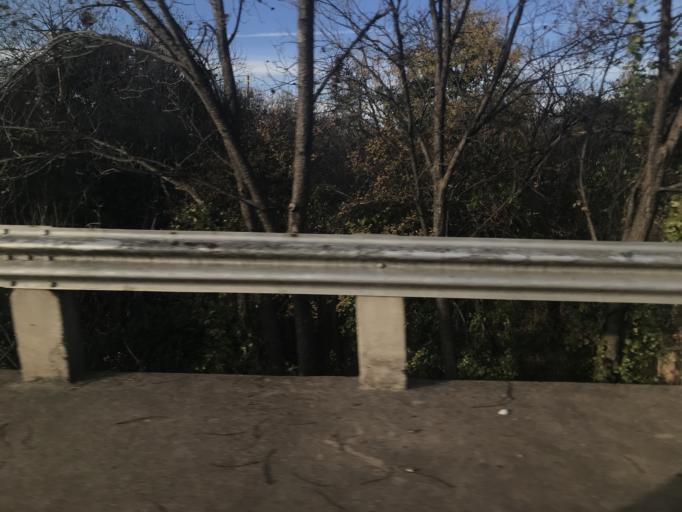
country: US
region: Texas
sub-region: Taylor County
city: Abilene
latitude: 32.4324
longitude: -99.7749
